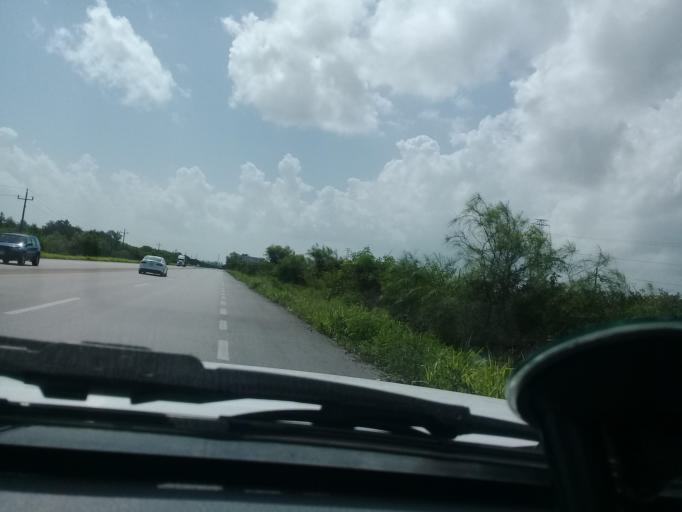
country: MX
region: Veracruz
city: Moralillo
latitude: 22.2132
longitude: -97.9720
